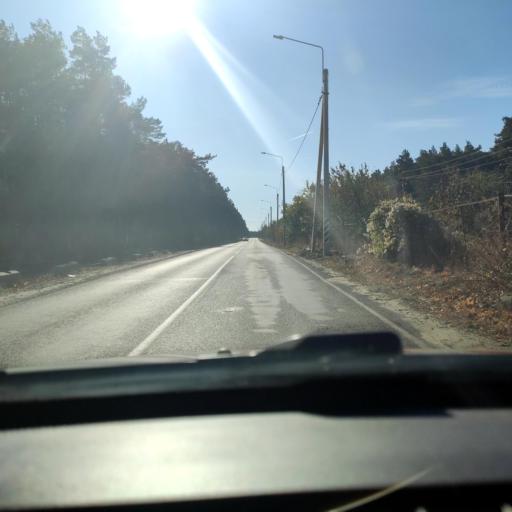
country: RU
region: Voronezj
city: Shilovo
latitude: 51.5364
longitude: 39.1391
